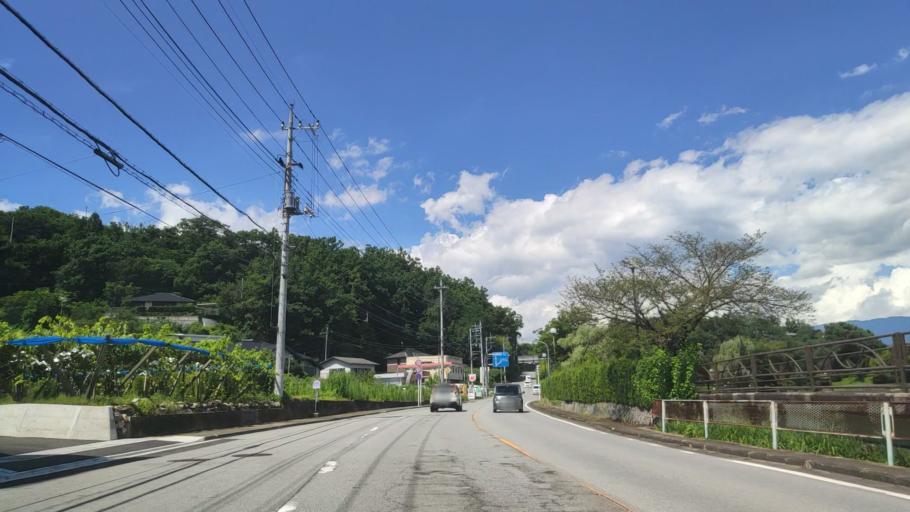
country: JP
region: Yamanashi
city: Enzan
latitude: 35.6938
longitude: 138.6810
